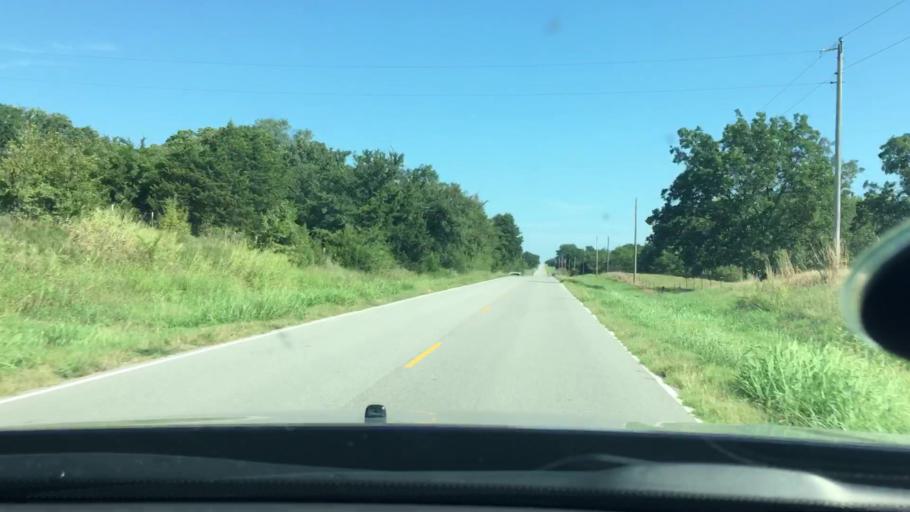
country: US
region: Oklahoma
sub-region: Johnston County
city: Tishomingo
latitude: 34.2865
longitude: -96.5487
